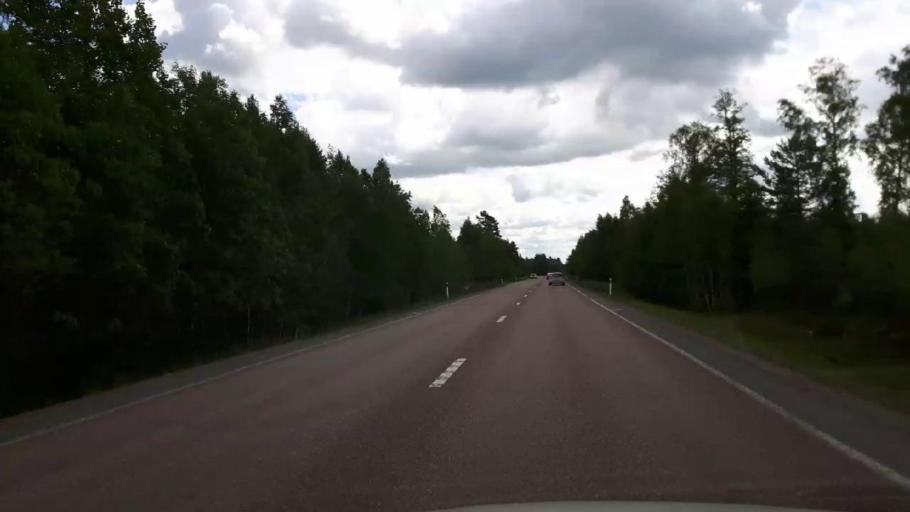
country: SE
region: Dalarna
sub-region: Saters Kommun
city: Saeter
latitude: 60.4932
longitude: 15.7608
